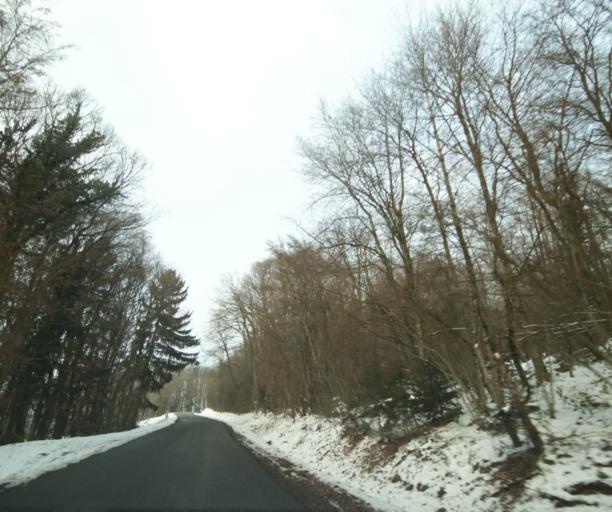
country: FR
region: Rhone-Alpes
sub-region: Departement de la Haute-Savoie
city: Monnetier-Mornex
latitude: 46.1406
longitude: 6.2295
